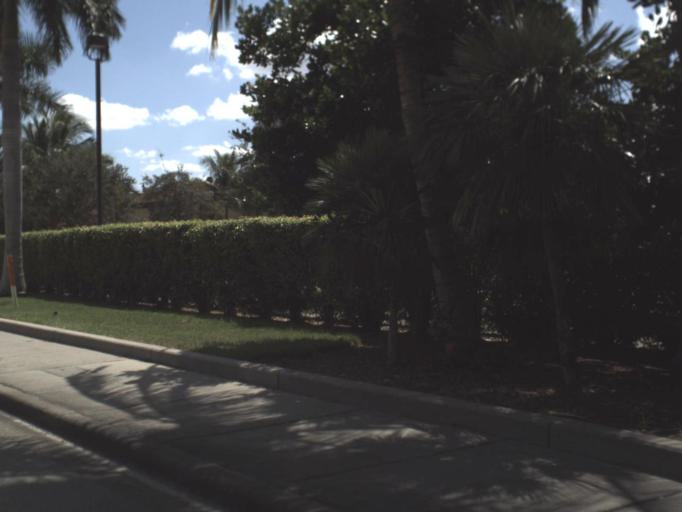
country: US
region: Florida
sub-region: Collier County
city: Naples
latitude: 26.1379
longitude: -81.7825
